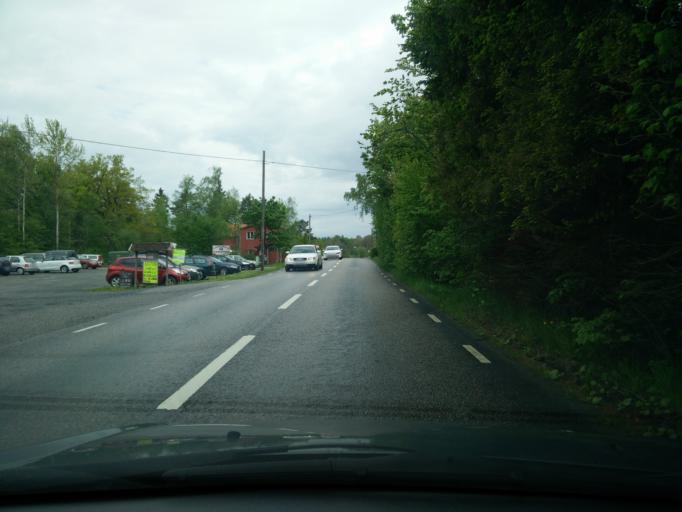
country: SE
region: Stockholm
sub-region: Norrtalje Kommun
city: Bjorko
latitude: 59.8128
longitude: 18.8933
